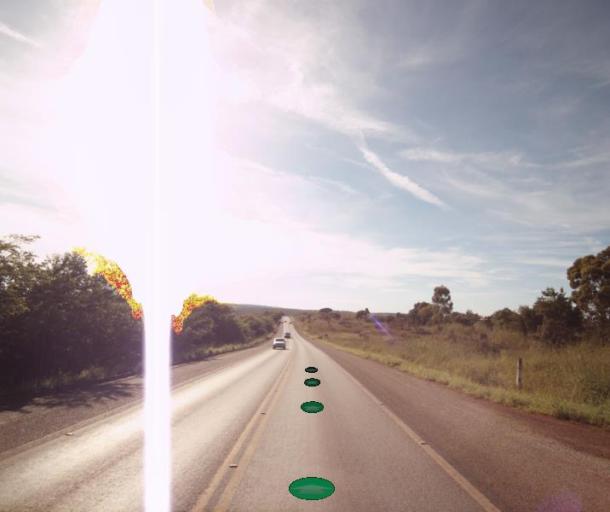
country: BR
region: Federal District
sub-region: Brasilia
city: Brasilia
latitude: -15.7432
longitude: -48.3702
